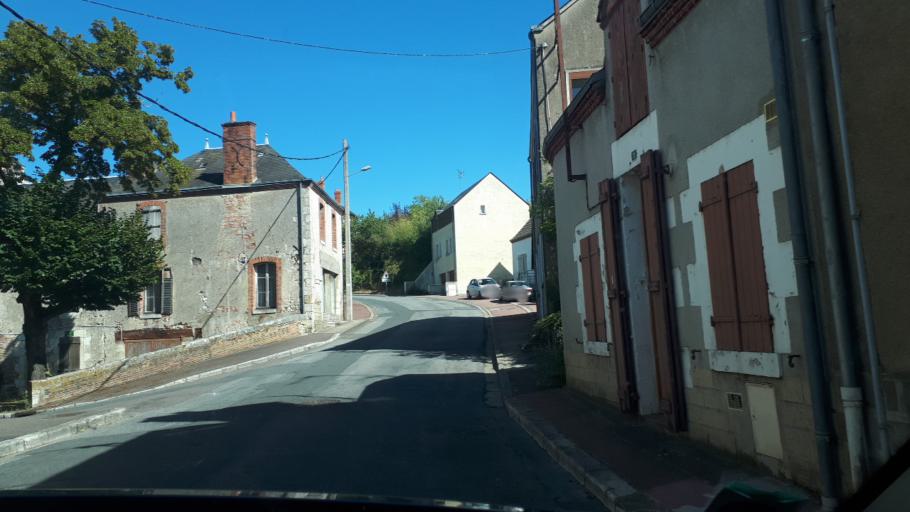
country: FR
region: Centre
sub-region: Departement du Loiret
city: Autry-le-Chatel
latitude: 47.5970
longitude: 2.6029
